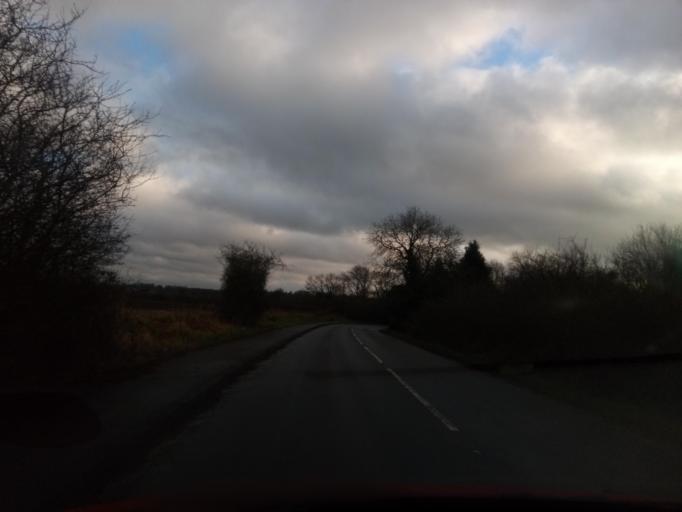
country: GB
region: England
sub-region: Derbyshire
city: Melbourne
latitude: 52.8480
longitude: -1.4101
